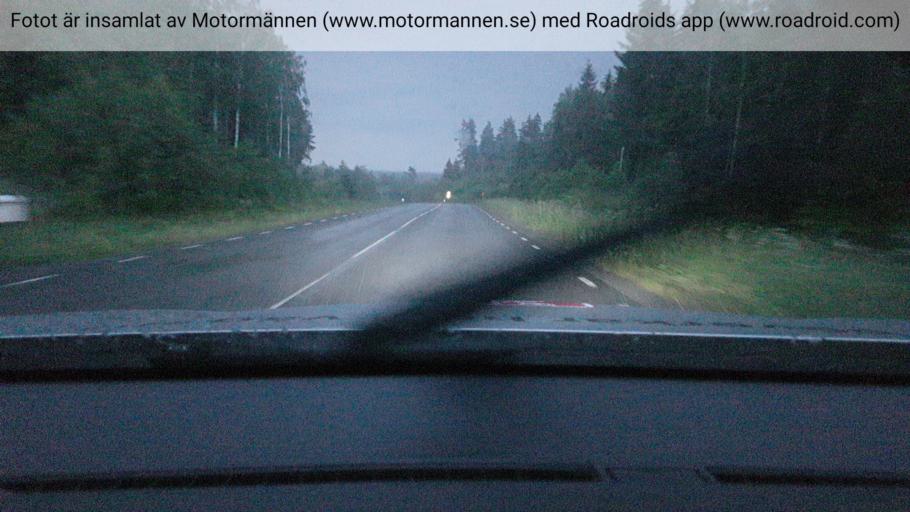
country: SE
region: Vaestra Goetaland
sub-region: Skovde Kommun
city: Stopen
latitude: 58.5373
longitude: 13.7309
